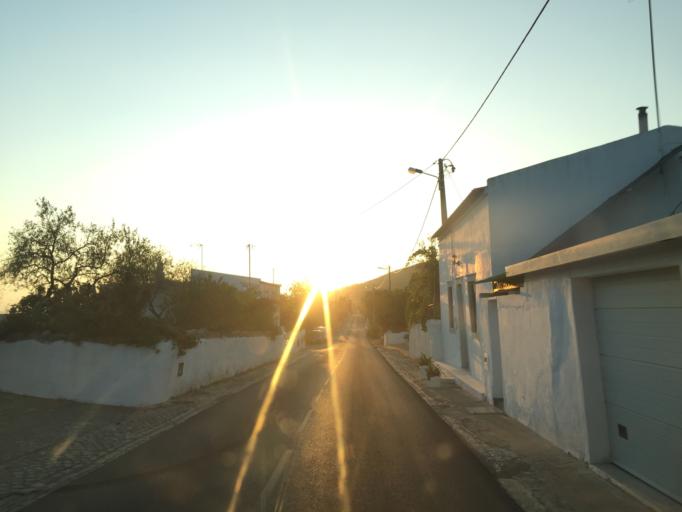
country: PT
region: Faro
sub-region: Faro
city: Santa Barbara de Nexe
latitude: 37.1042
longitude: -7.9671
